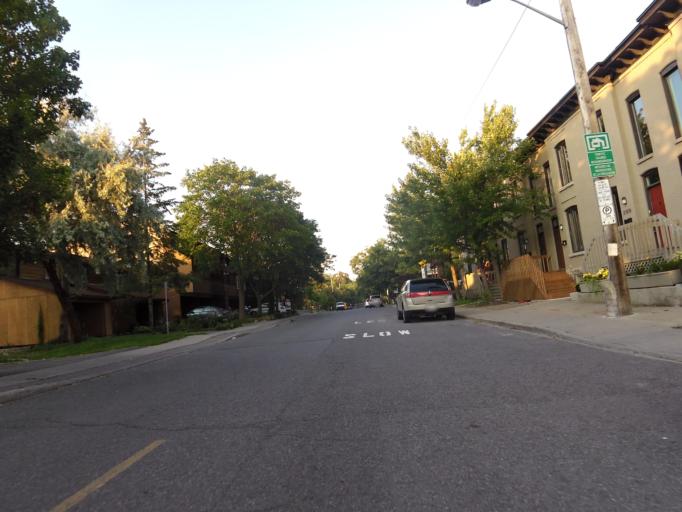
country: CA
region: Ontario
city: Ottawa
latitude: 45.4104
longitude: -75.7151
